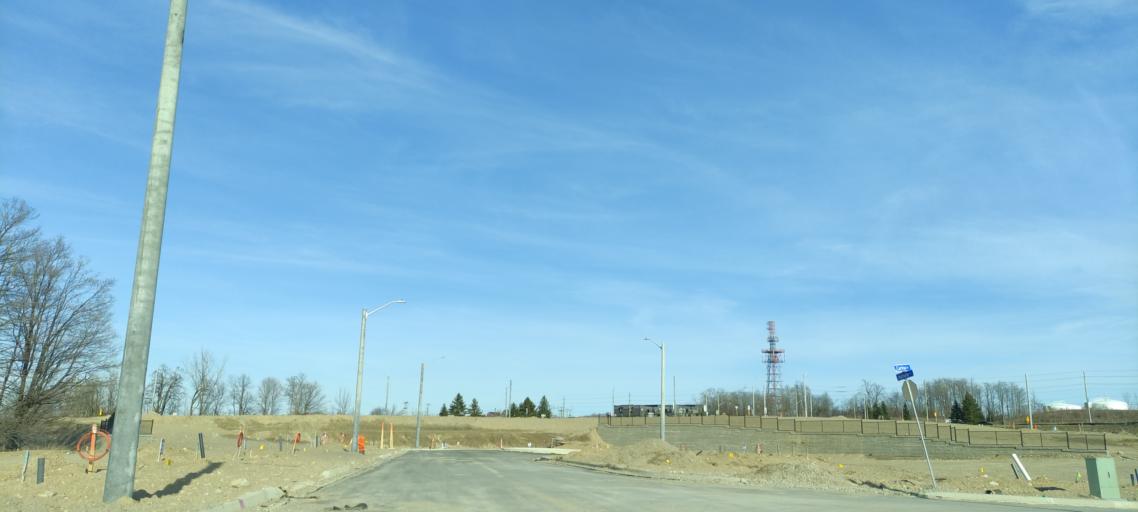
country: CA
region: Ontario
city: Kitchener
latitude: 43.4047
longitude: -80.5366
